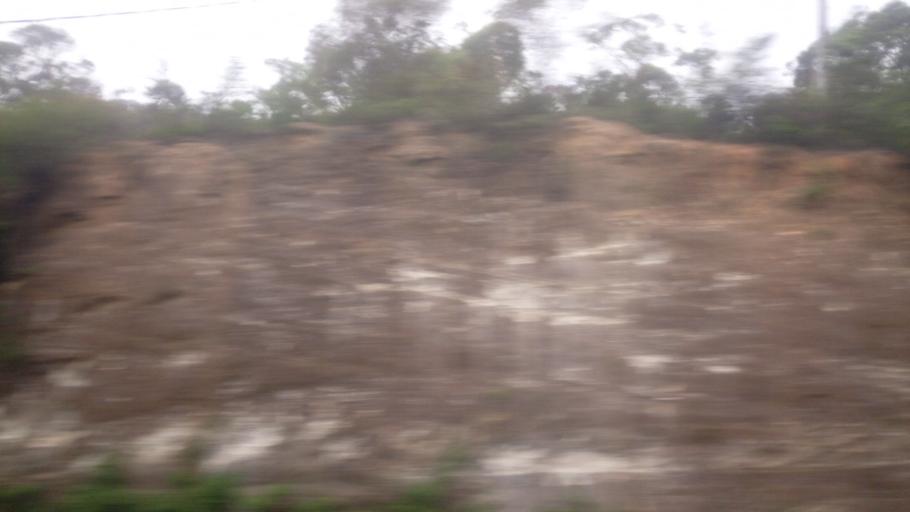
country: AU
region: New South Wales
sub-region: Blue Mountains Municipality
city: Lawson
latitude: -33.7233
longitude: 150.3866
